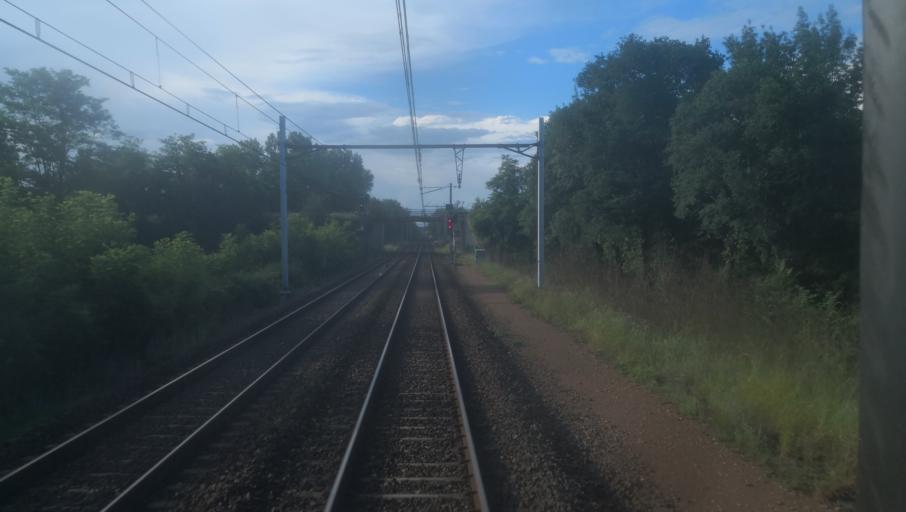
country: FR
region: Centre
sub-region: Departement du Loir-et-Cher
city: Salbris
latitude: 47.4292
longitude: 2.0467
